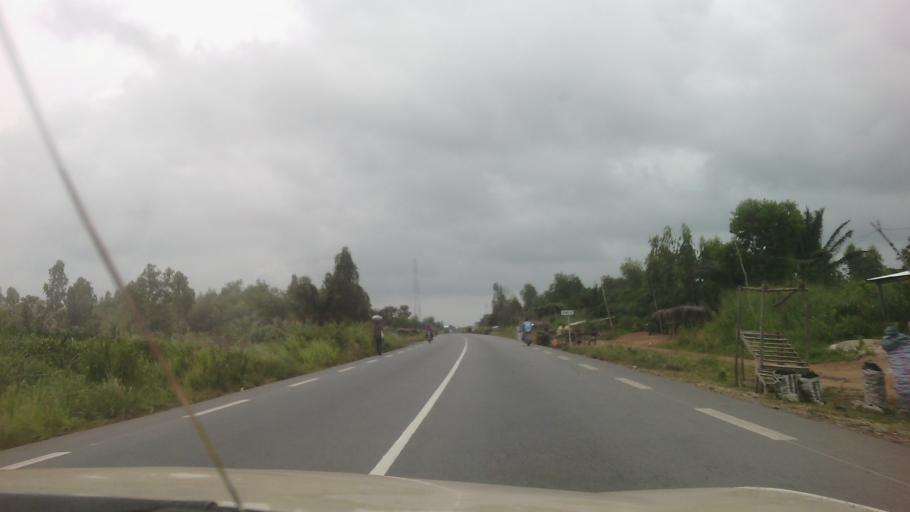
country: BJ
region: Mono
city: Come
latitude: 6.3953
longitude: 1.9832
